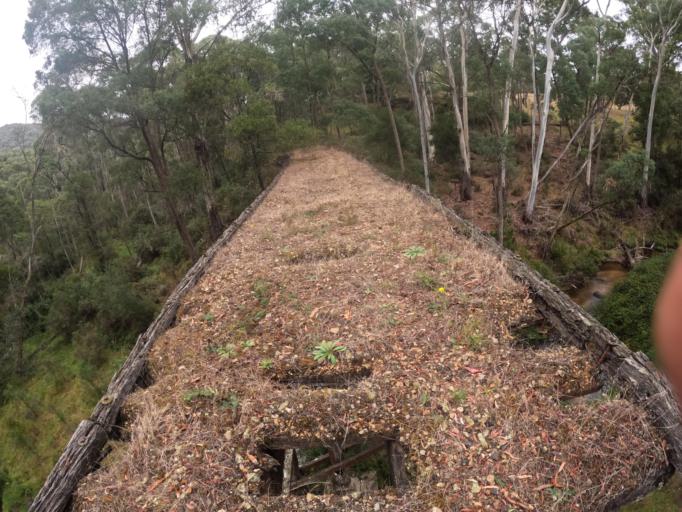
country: AU
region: New South Wales
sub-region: Greater Hume Shire
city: Holbrook
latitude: -36.2306
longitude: 147.6033
